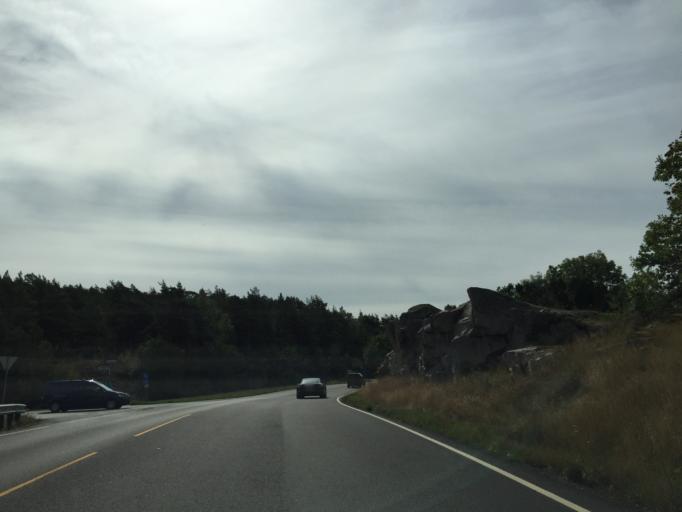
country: NO
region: Ostfold
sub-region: Fredrikstad
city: Fredrikstad
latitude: 59.1600
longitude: 10.9315
